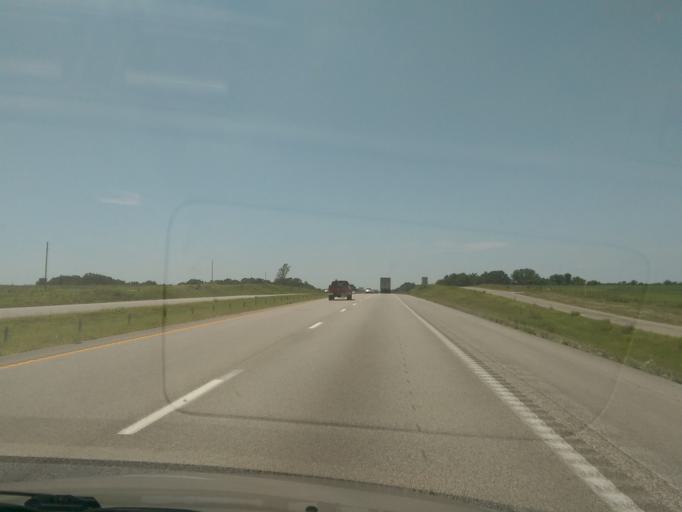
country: US
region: Missouri
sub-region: Saline County
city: Sweet Springs
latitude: 38.9720
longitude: -93.2809
